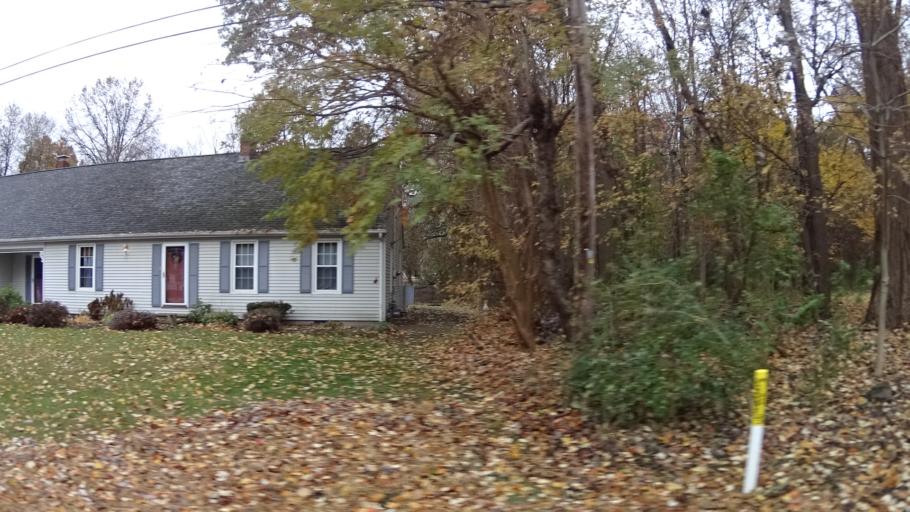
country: US
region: Ohio
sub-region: Lorain County
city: Elyria
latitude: 41.3962
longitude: -82.1349
